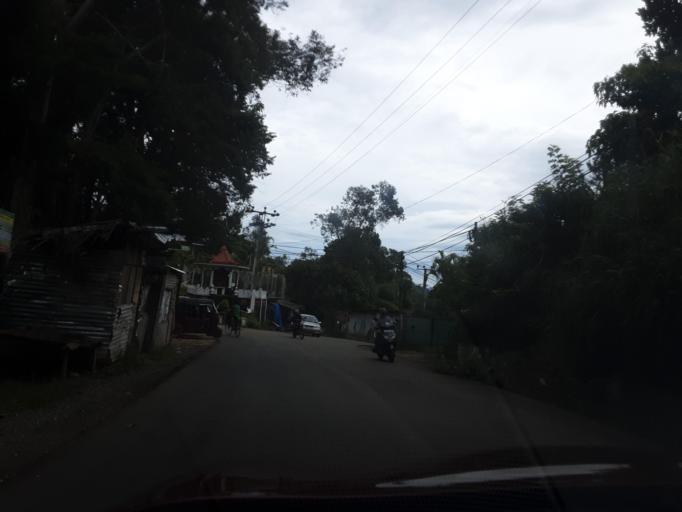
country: LK
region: Uva
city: Haputale
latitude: 6.8345
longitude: 80.9932
